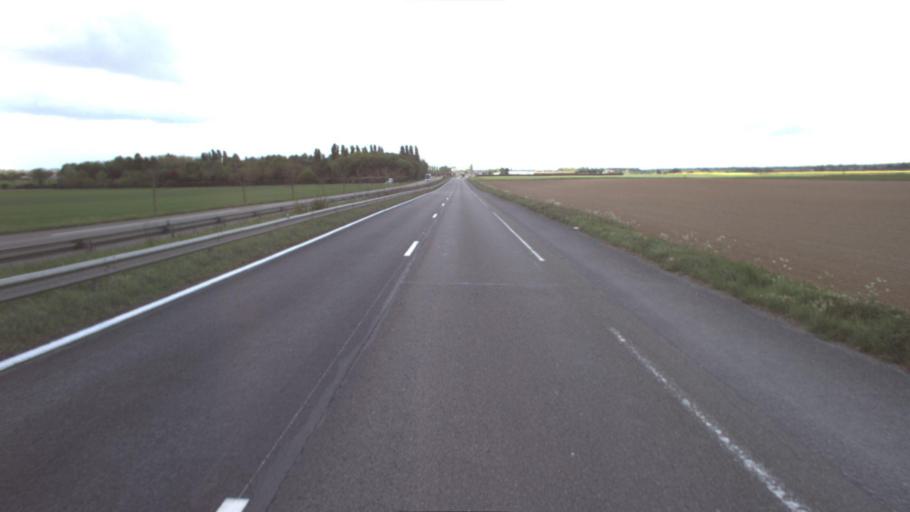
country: FR
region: Ile-de-France
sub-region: Departement de Seine-et-Marne
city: Rozay-en-Brie
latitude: 48.6865
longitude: 2.9826
